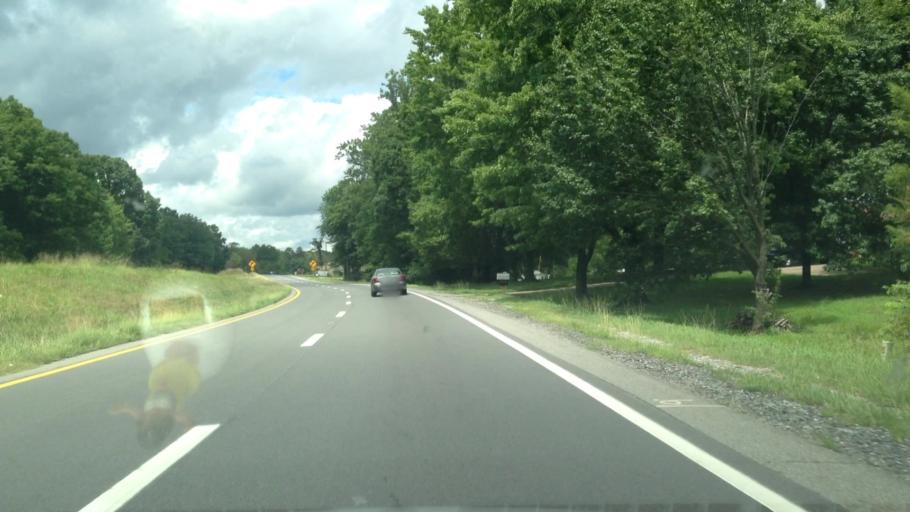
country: US
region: Virginia
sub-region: Henry County
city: Stanleytown
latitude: 36.8049
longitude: -79.9375
